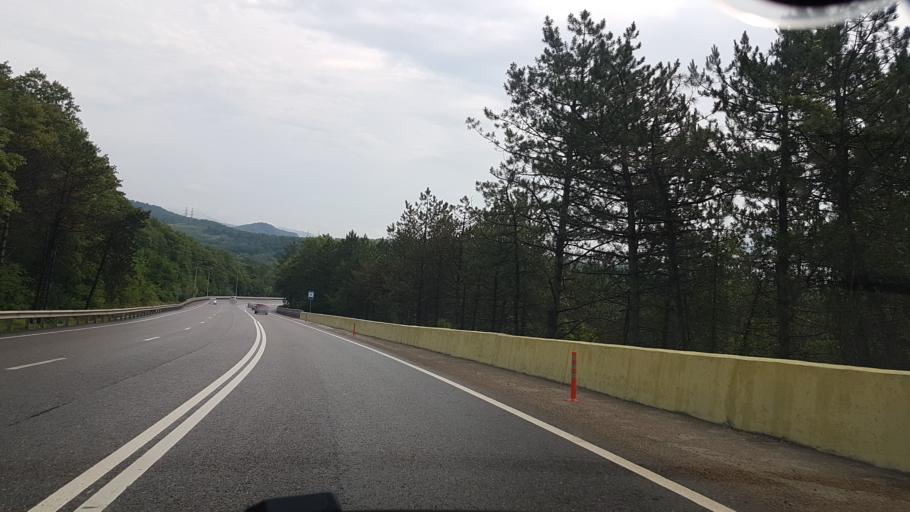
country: RU
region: Krasnodarskiy
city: Dzhubga
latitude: 44.4275
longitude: 38.7625
